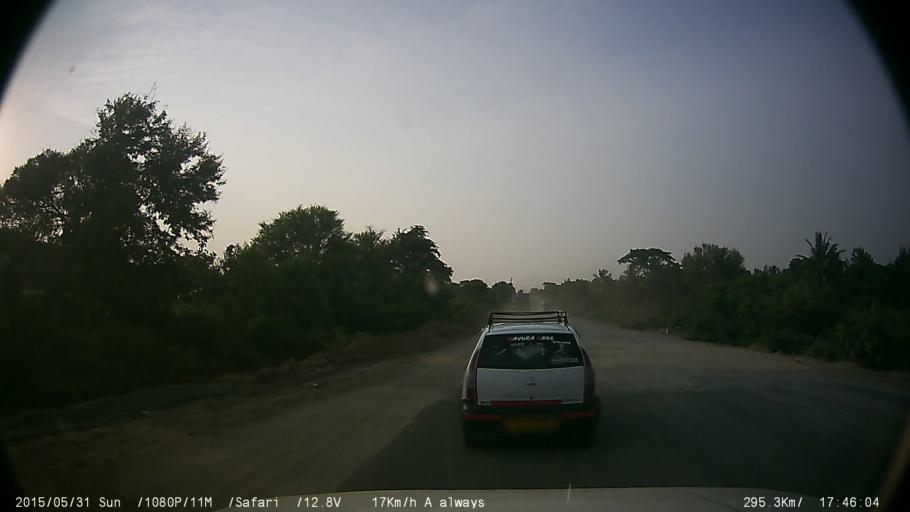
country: IN
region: Karnataka
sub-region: Chamrajnagar
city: Gundlupet
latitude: 11.9557
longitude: 76.6705
